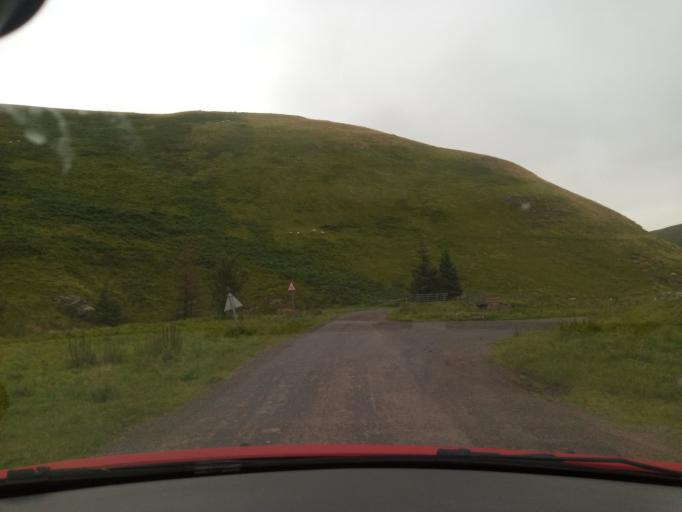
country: GB
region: England
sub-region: Northumberland
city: Rochester
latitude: 55.3972
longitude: -2.2456
